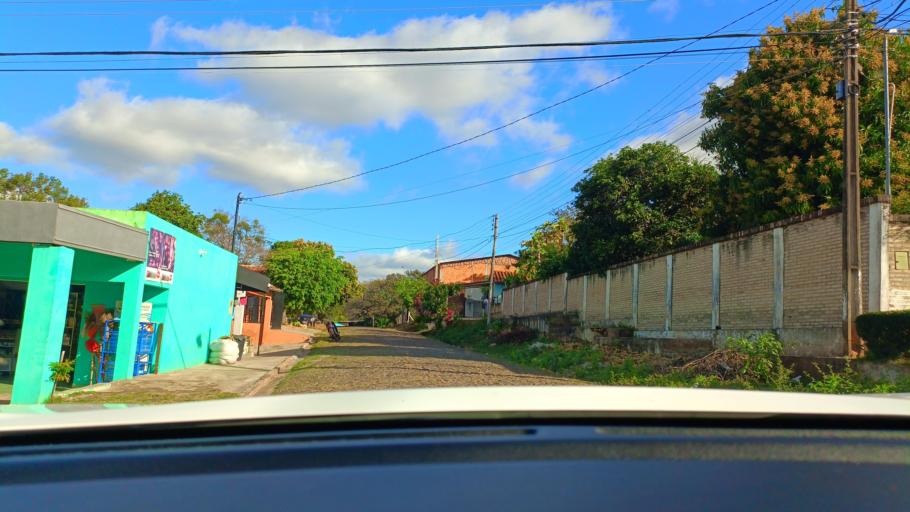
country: PY
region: San Pedro
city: Guayaybi
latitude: -24.6723
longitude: -56.4392
